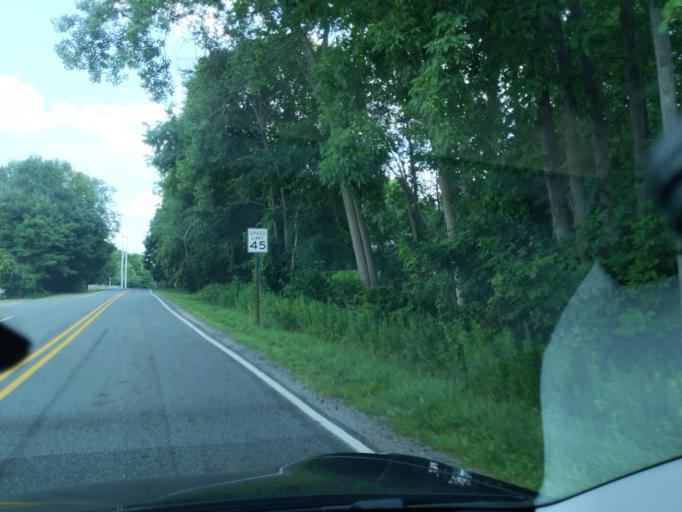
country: US
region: Michigan
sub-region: Kent County
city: Forest Hills
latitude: 42.9806
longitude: -85.5365
